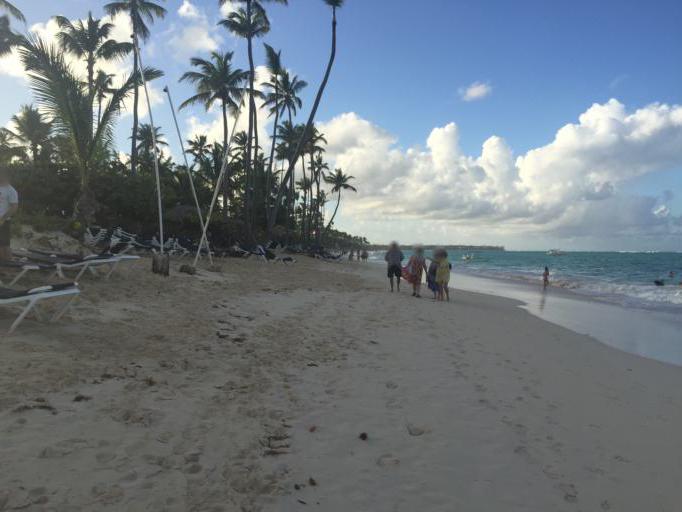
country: DO
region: San Juan
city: Punta Cana
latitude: 18.6949
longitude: -68.4263
